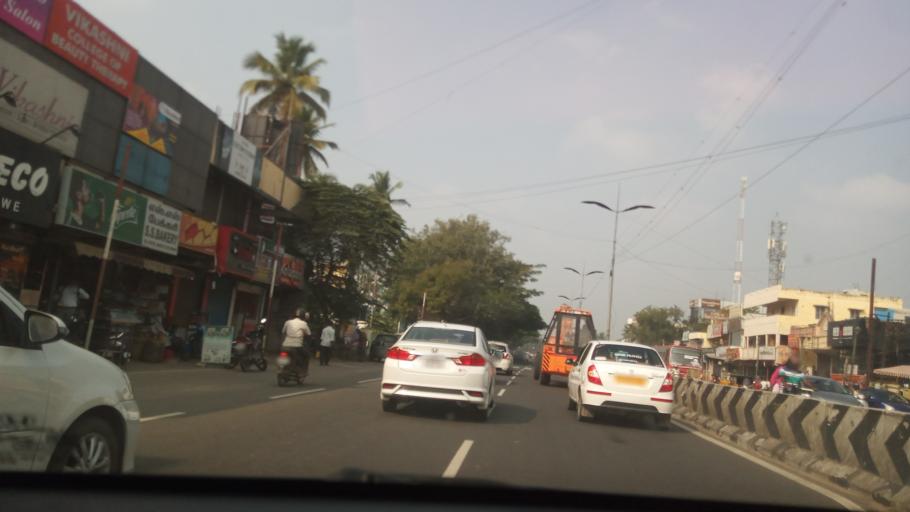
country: IN
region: Tamil Nadu
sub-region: Coimbatore
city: Singanallur
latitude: 11.0255
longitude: 77.0154
